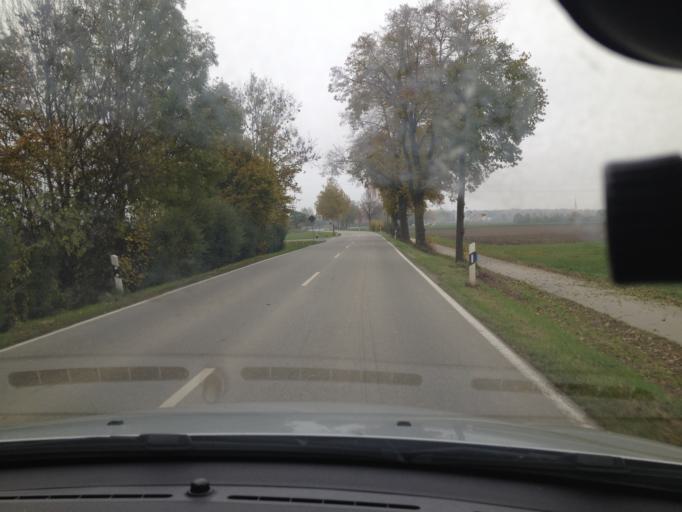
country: DE
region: Bavaria
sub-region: Swabia
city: Hiltenfingen
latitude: 48.1919
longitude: 10.7292
